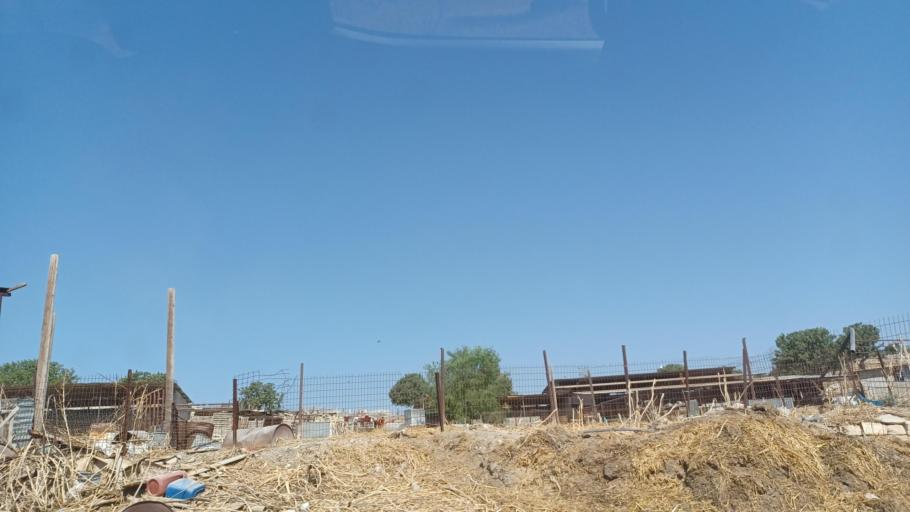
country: CY
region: Limassol
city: Pissouri
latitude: 34.6763
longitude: 32.7149
